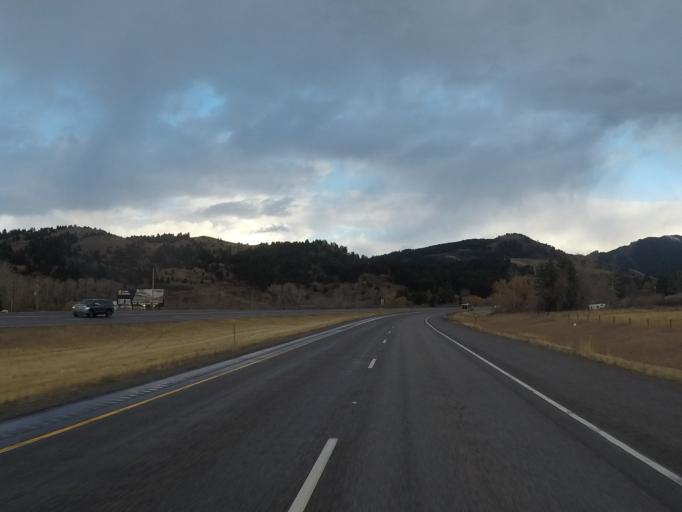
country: US
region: Montana
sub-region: Gallatin County
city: Bozeman
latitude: 45.6615
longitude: -110.9559
